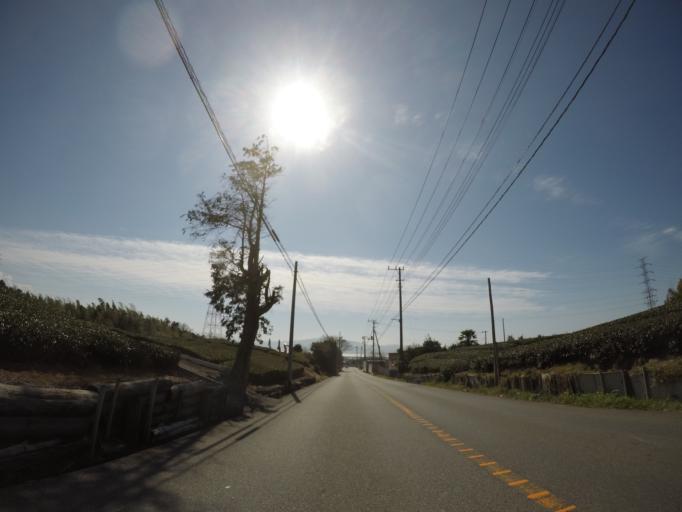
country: JP
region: Shizuoka
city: Numazu
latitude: 35.1360
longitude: 138.8361
